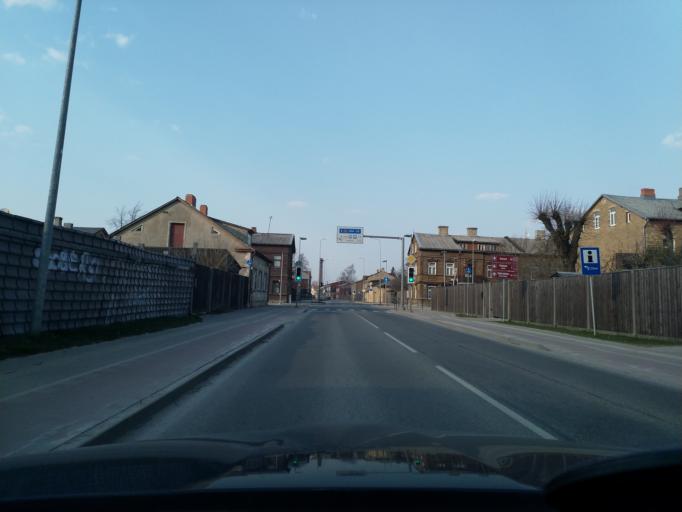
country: LV
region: Liepaja
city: Liepaja
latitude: 56.5052
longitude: 21.0243
